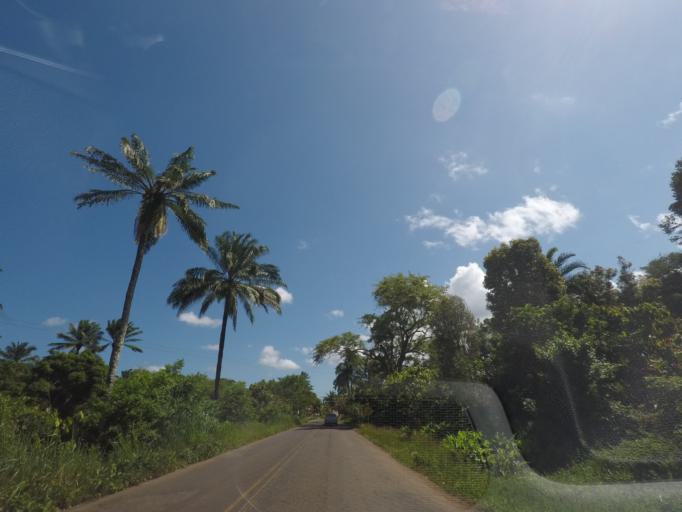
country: BR
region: Bahia
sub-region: Taperoa
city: Taperoa
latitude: -13.5572
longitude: -39.1046
